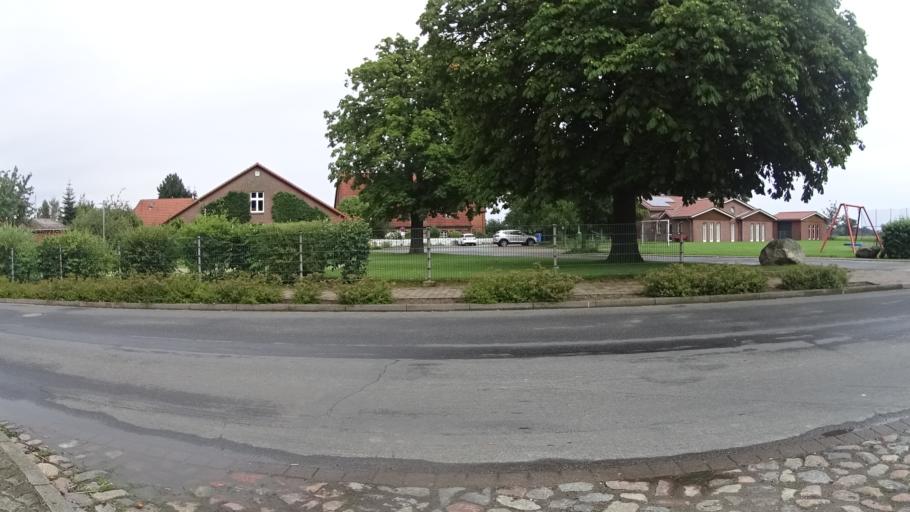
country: DE
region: Schleswig-Holstein
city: Schiphorst
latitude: 53.7108
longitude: 10.4618
